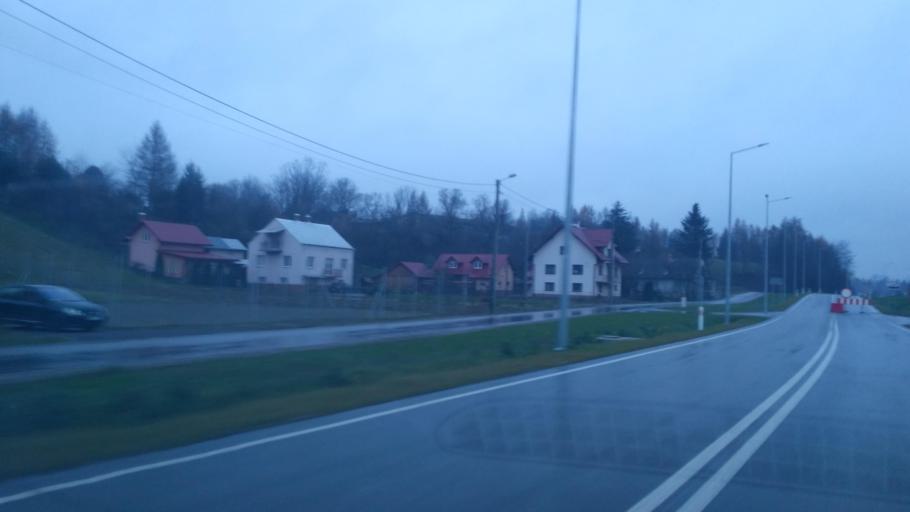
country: PL
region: Subcarpathian Voivodeship
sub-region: Powiat rzeszowski
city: Dynow
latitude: 49.8044
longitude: 22.2394
